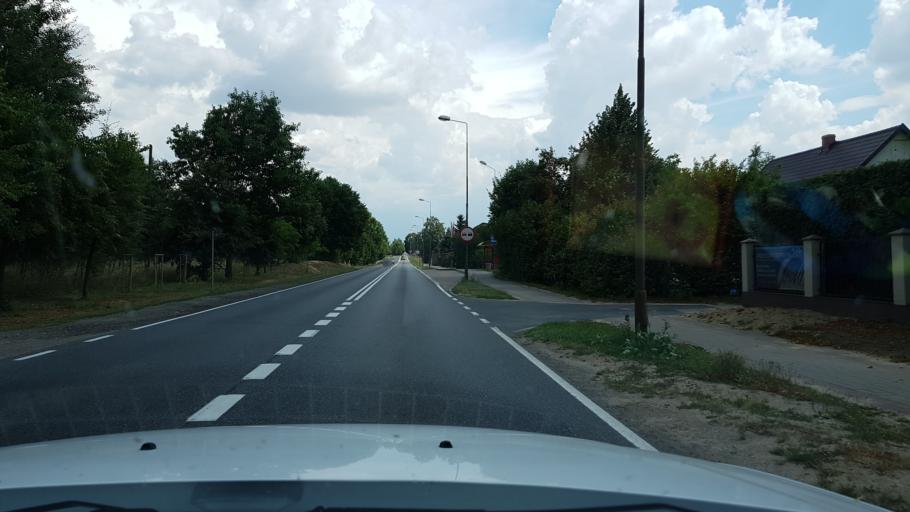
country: PL
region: West Pomeranian Voivodeship
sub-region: Powiat walecki
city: Walcz
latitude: 53.2881
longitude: 16.4394
